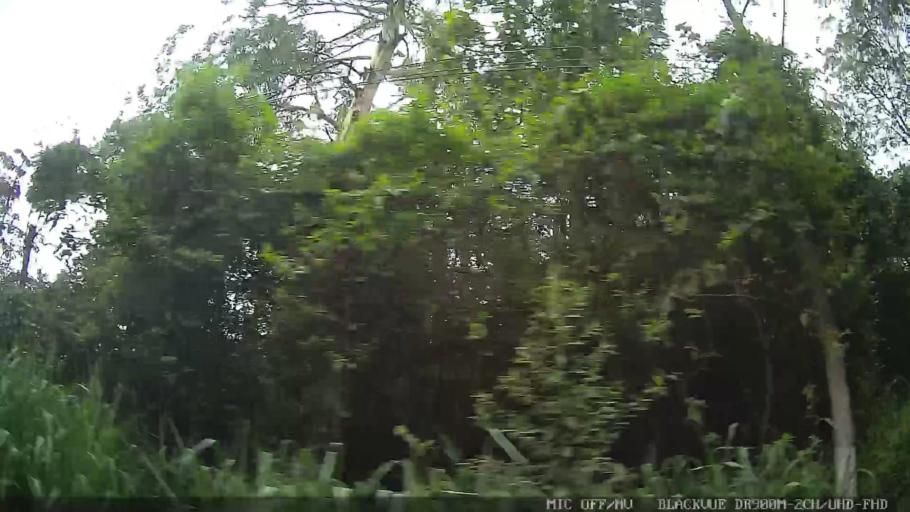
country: BR
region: Sao Paulo
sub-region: Osasco
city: Osasco
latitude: -23.4696
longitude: -46.7358
